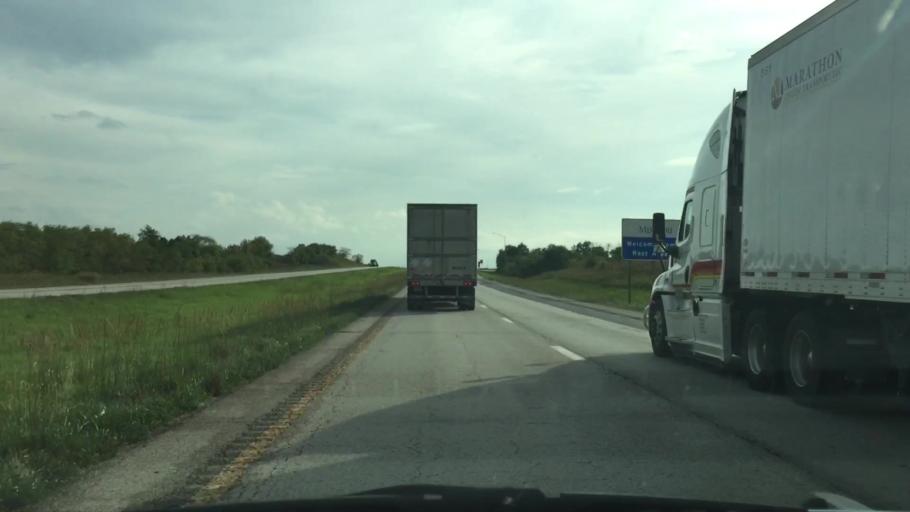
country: US
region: Iowa
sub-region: Decatur County
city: Lamoni
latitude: 40.5549
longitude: -93.9521
